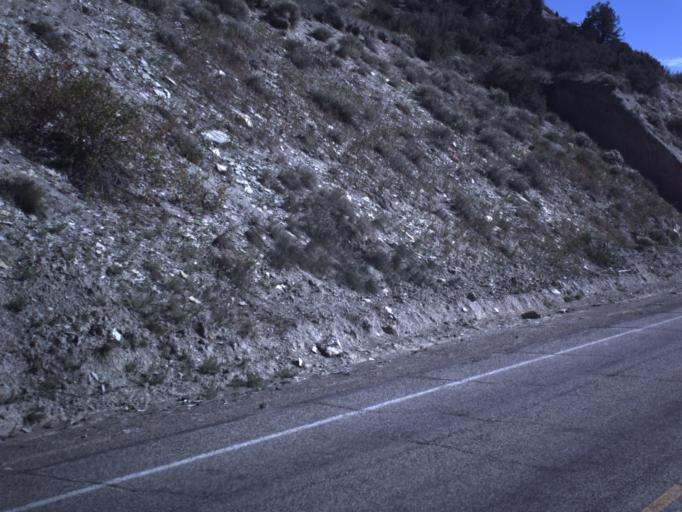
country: US
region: Utah
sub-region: Carbon County
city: Helper
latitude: 39.9077
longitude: -110.7069
